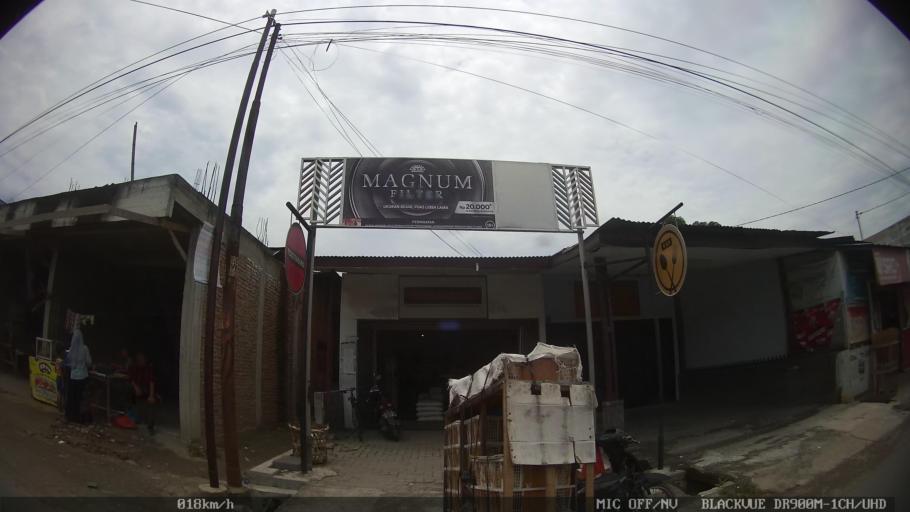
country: ID
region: North Sumatra
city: Sunggal
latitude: 3.6101
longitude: 98.5798
